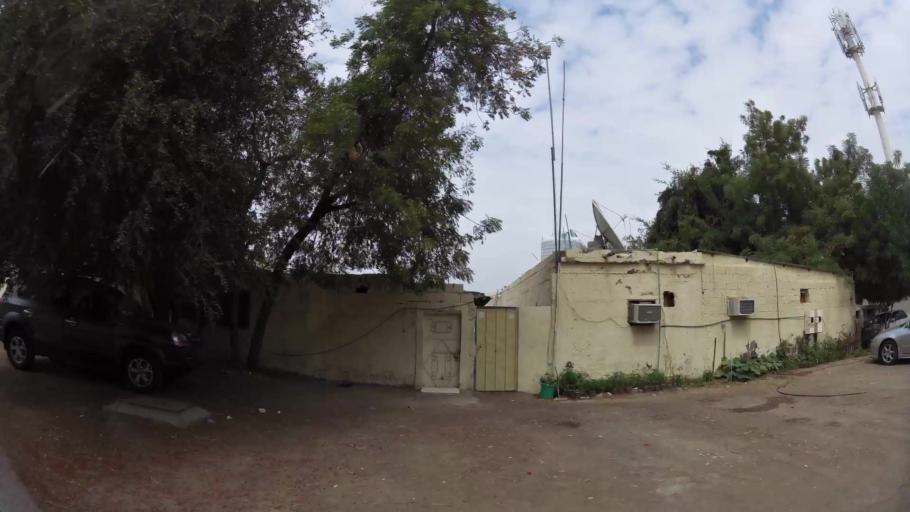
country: OM
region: Al Buraimi
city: Al Buraymi
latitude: 24.2163
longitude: 55.7870
